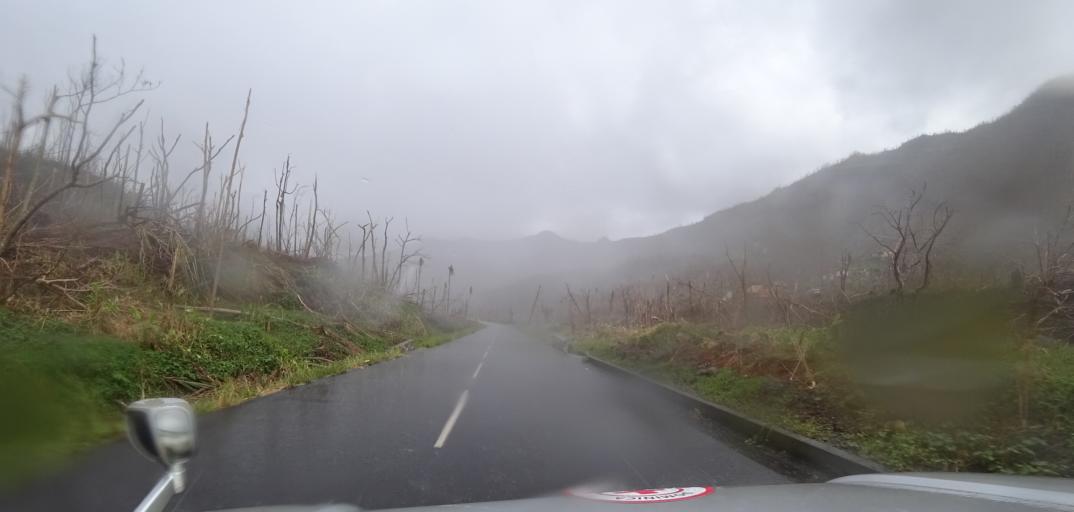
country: DM
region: Saint David
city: Castle Bruce
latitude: 15.4829
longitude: -61.2810
